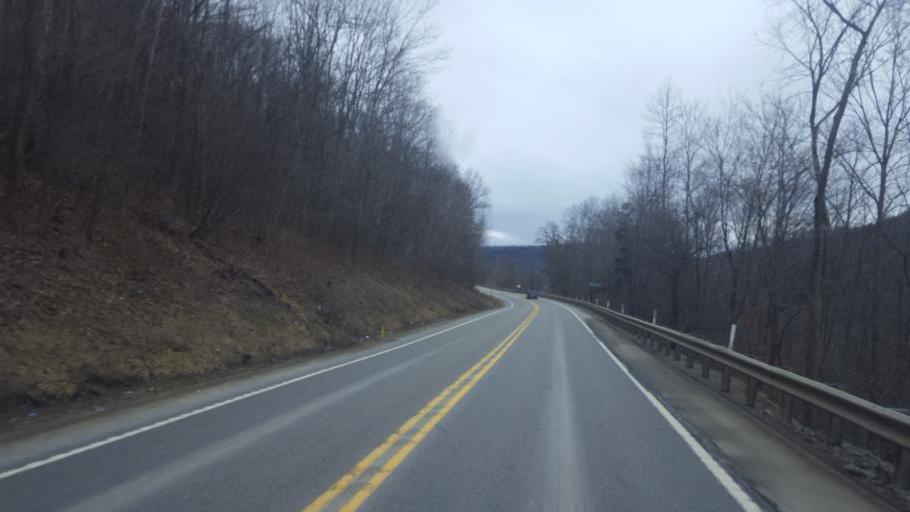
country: US
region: Pennsylvania
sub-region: Potter County
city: Coudersport
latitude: 41.7541
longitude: -78.1068
